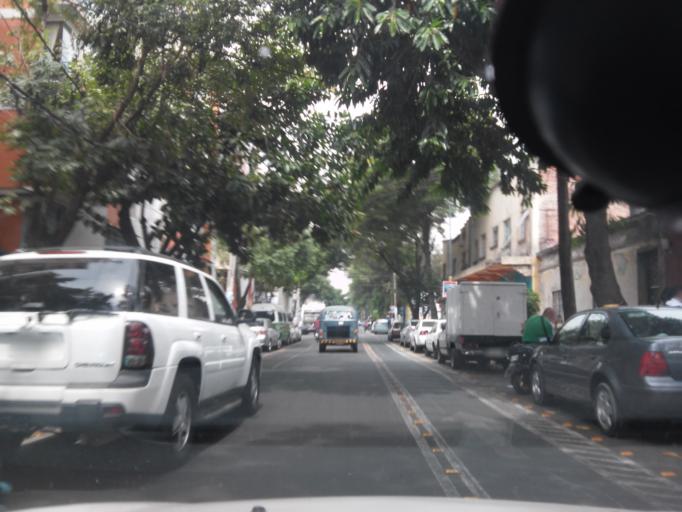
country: MX
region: Mexico City
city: Cuauhtemoc
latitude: 19.4440
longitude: -99.1714
